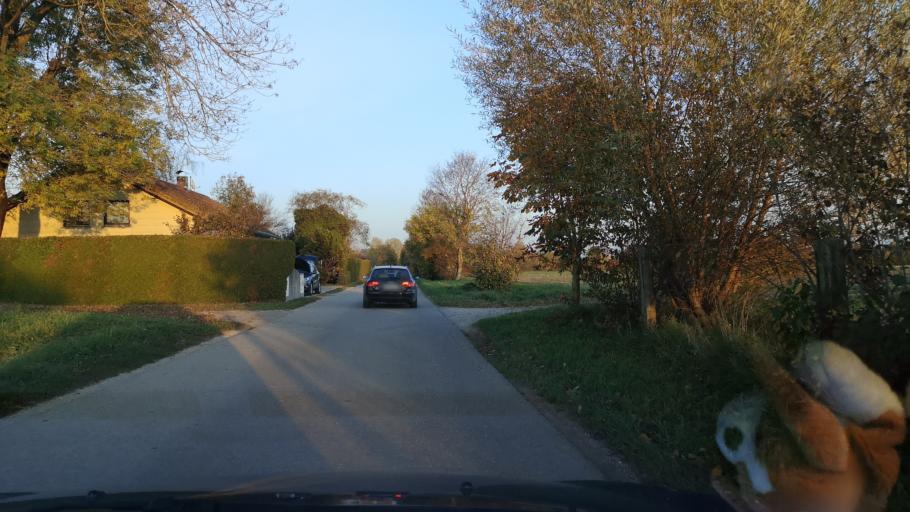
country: DE
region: Bavaria
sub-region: Upper Bavaria
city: Ismaning
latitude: 48.2452
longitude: 11.7279
